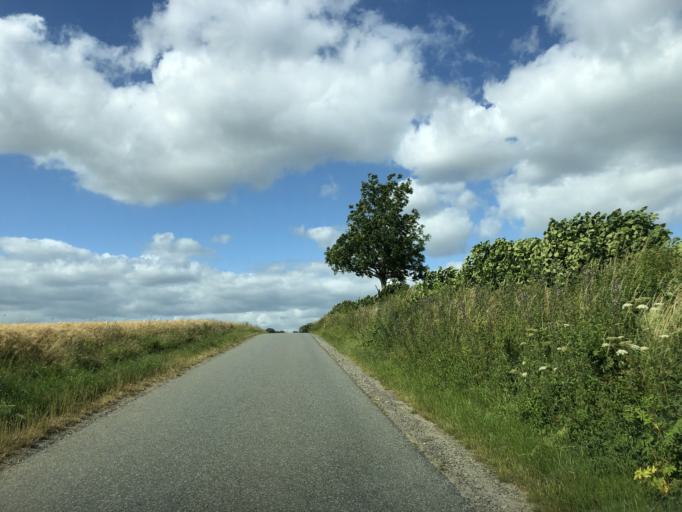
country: DK
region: South Denmark
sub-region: Vejle Kommune
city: Brejning
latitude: 55.6684
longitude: 9.6494
